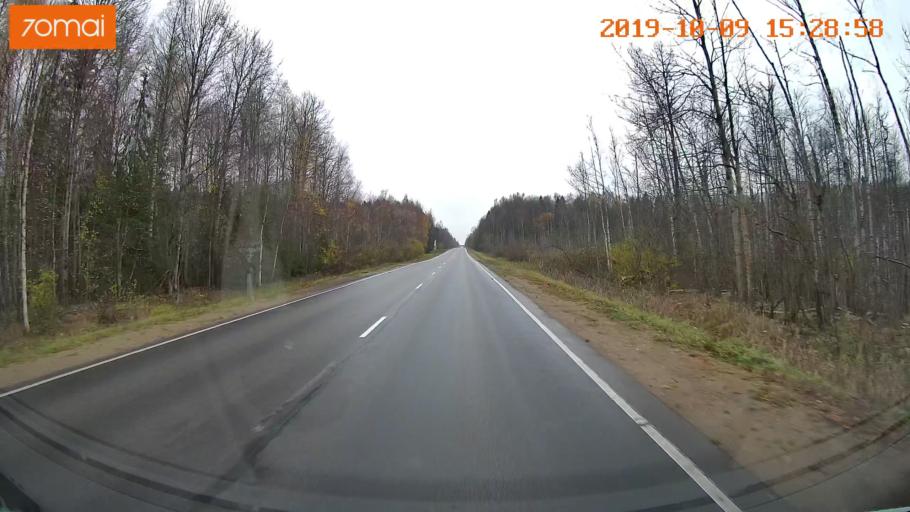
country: RU
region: Kostroma
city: Susanino
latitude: 57.9970
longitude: 41.3510
